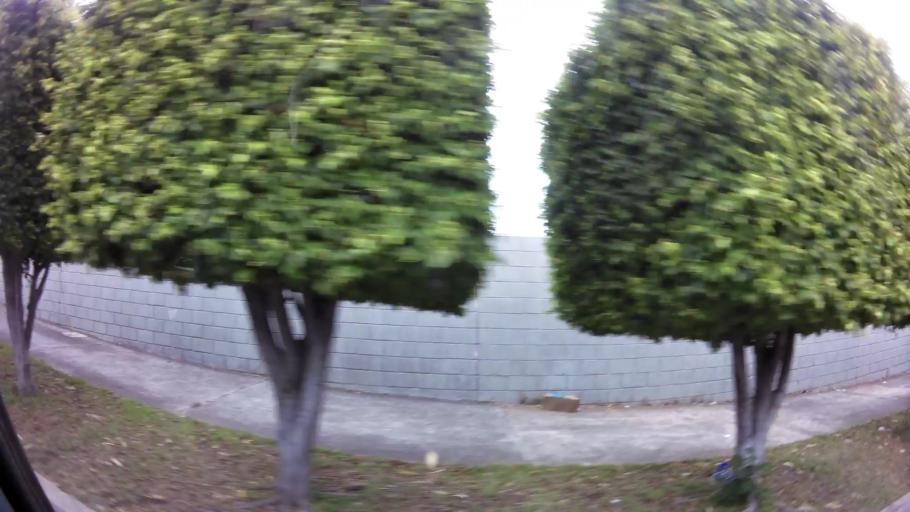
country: HN
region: Francisco Morazan
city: Tegucigalpa
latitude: 14.0768
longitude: -87.1831
